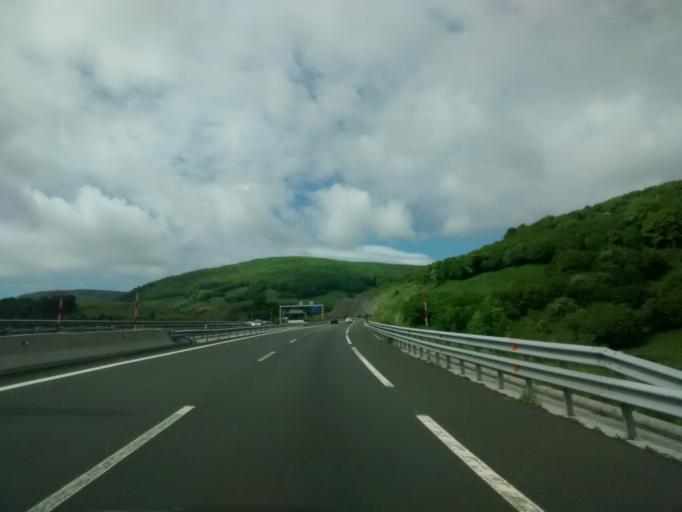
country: ES
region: Cantabria
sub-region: Provincia de Cantabria
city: Pesquera
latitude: 43.0855
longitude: -4.0818
